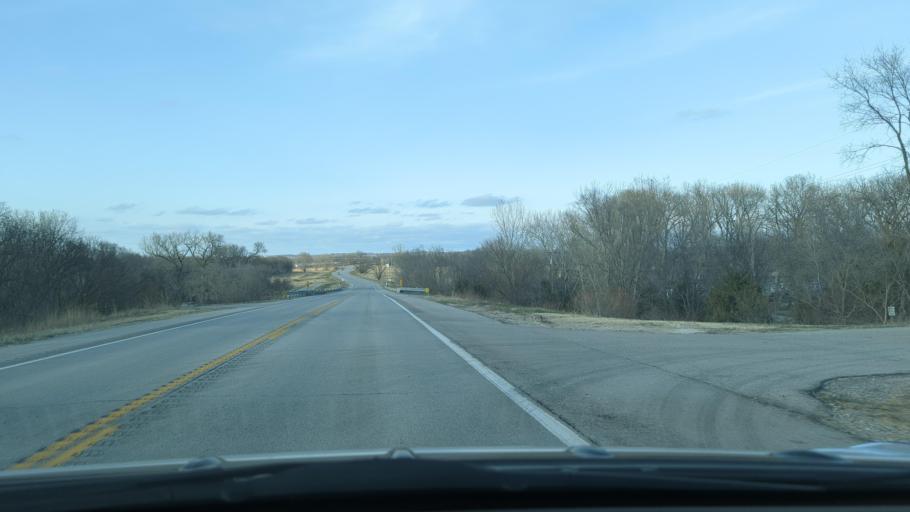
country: US
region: Nebraska
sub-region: Saunders County
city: Ashland
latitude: 41.0505
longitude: -96.3399
